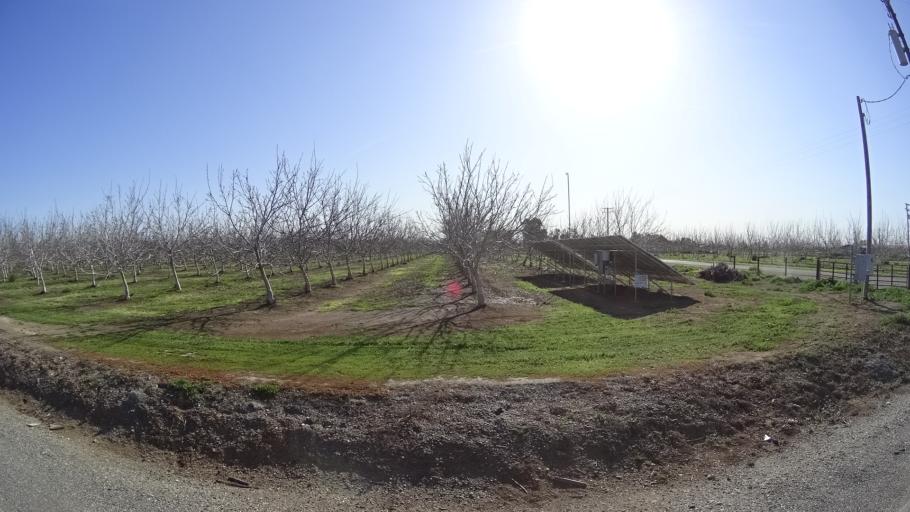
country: US
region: California
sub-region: Glenn County
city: Orland
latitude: 39.7827
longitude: -122.1041
